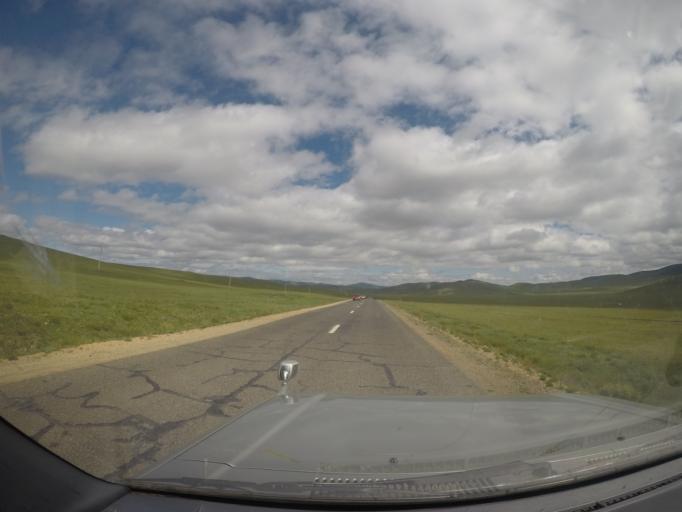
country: MN
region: Hentiy
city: Modot
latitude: 47.7691
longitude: 108.8757
